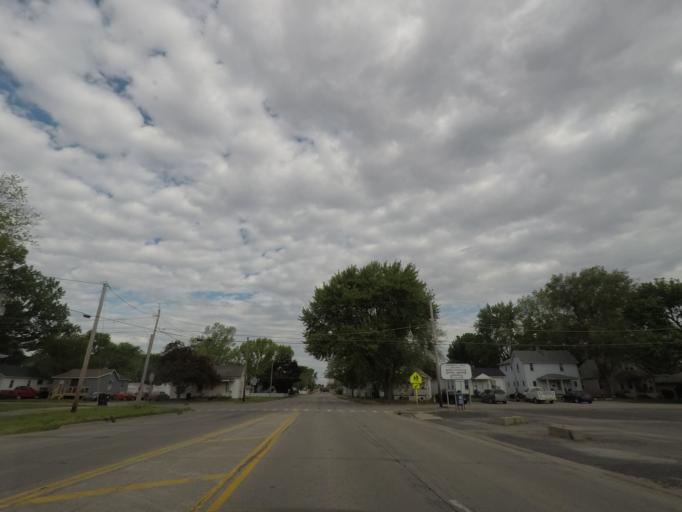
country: US
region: Illinois
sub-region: Logan County
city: Lincoln
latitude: 40.1492
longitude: -89.3536
